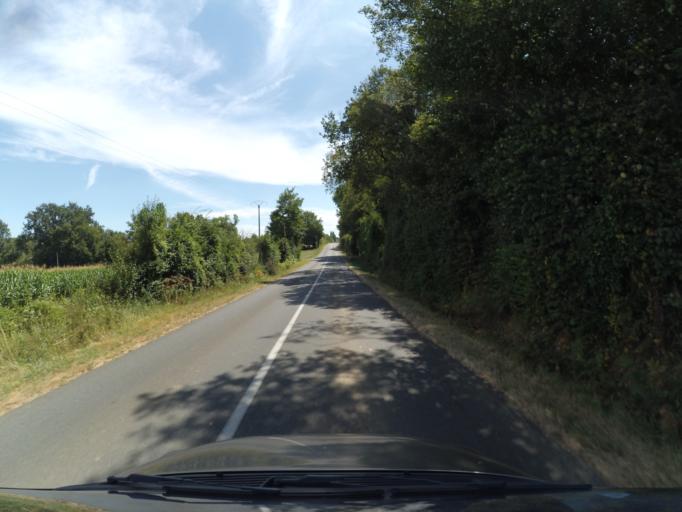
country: FR
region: Poitou-Charentes
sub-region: Departement de la Vienne
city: Usson-du-Poitou
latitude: 46.2783
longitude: 0.5172
